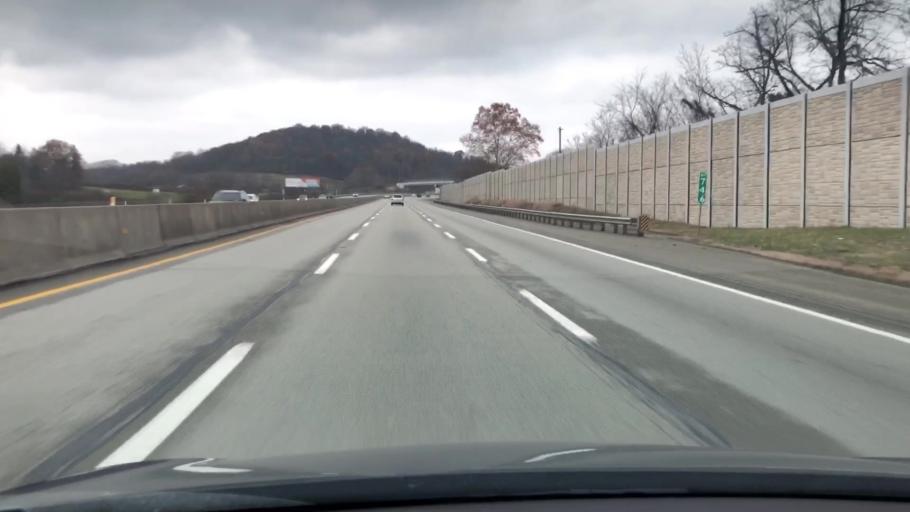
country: US
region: Pennsylvania
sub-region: Westmoreland County
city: New Stanton
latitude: 40.2300
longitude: -79.6152
